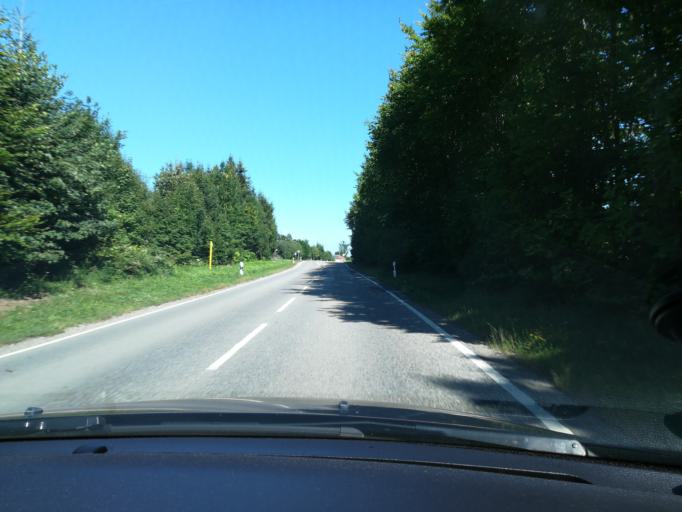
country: DE
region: Bavaria
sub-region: Upper Bavaria
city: Eggstatt
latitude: 47.9096
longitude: 12.3646
